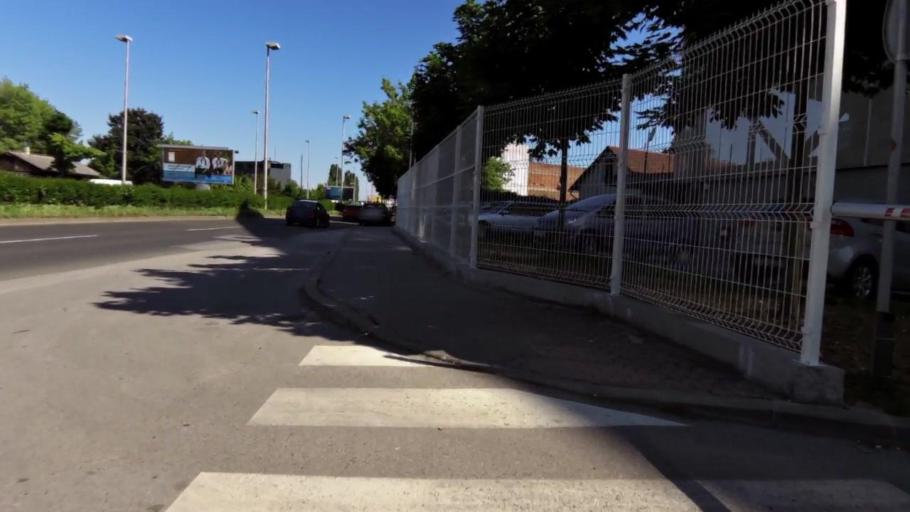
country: HR
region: Grad Zagreb
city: Novi Zagreb
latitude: 45.8007
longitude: 16.0126
